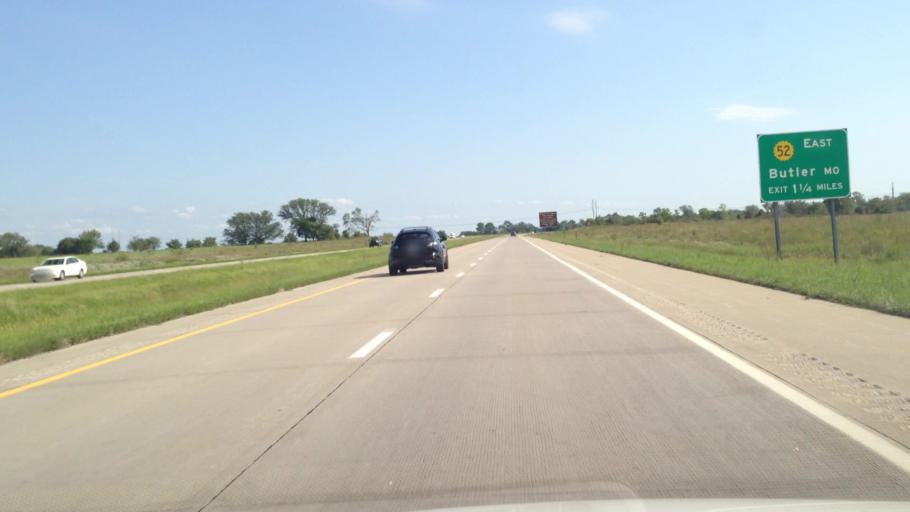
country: US
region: Kansas
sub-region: Linn County
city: Pleasanton
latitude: 38.2824
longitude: -94.6716
